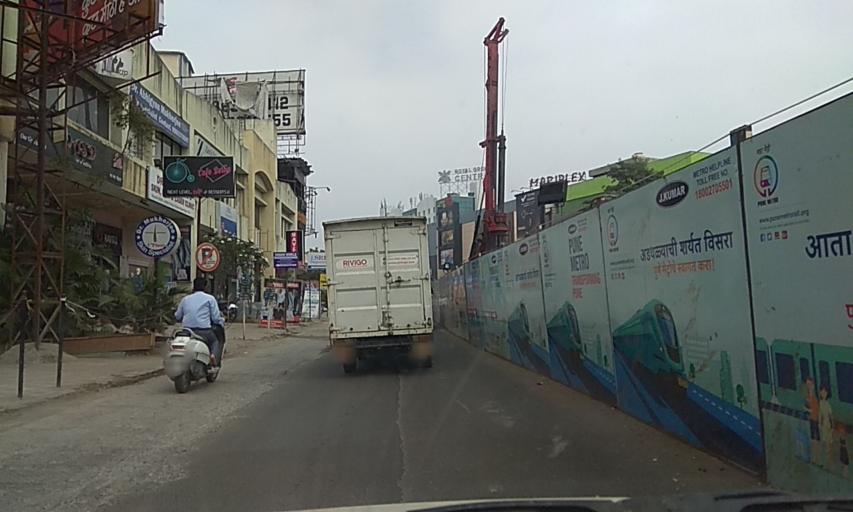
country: IN
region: Maharashtra
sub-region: Pune Division
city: Shivaji Nagar
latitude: 18.5444
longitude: 73.9056
